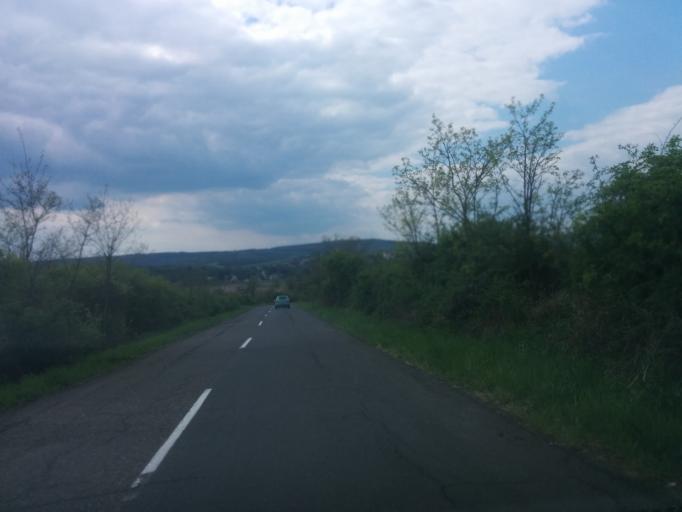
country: HU
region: Nograd
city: Palotas
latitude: 47.8272
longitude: 19.5497
